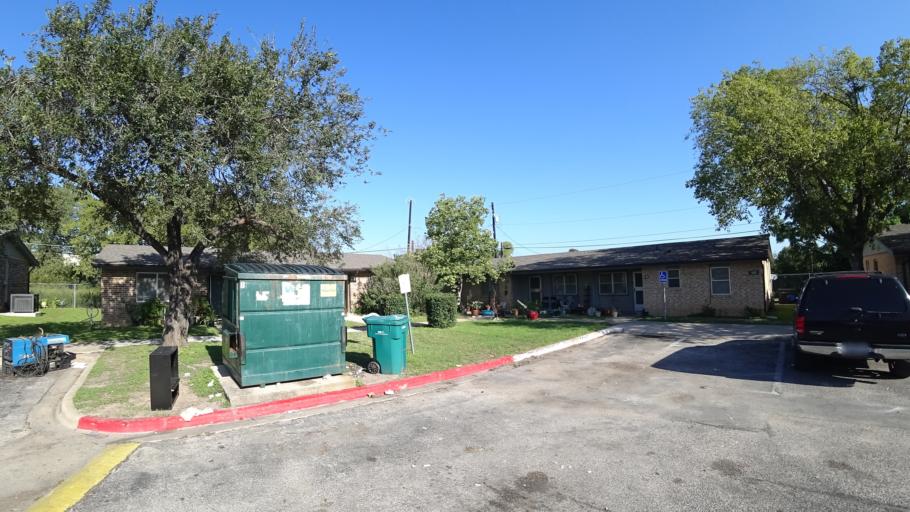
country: US
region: Texas
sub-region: Travis County
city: Austin
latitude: 30.3511
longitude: -97.7037
